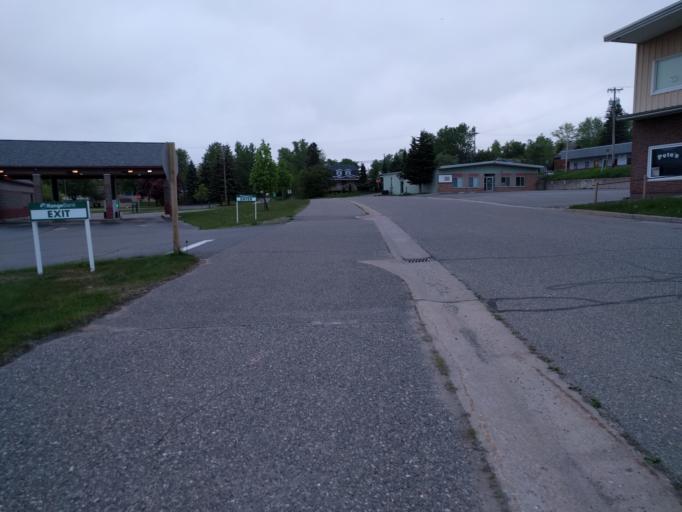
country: US
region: Michigan
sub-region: Marquette County
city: Trowbridge Park
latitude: 46.5470
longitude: -87.4190
